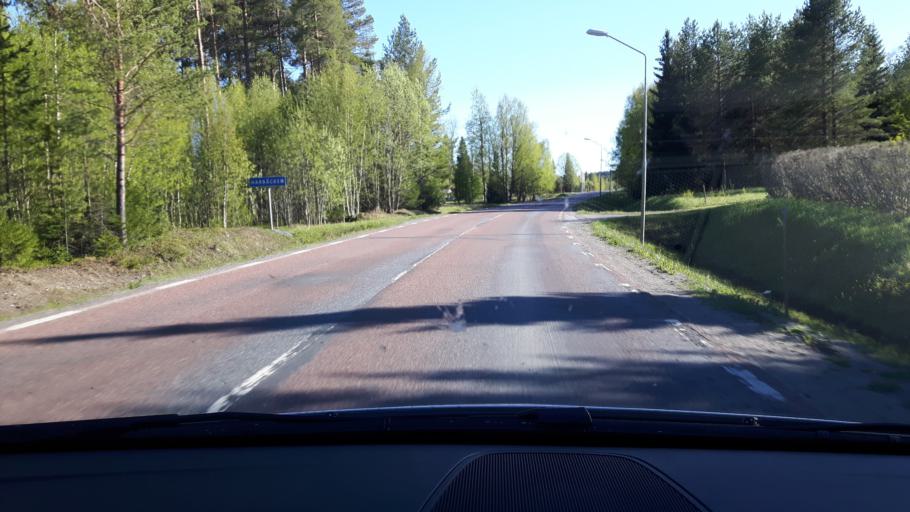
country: SE
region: Jaemtland
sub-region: Stroemsunds Kommun
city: Stroemsund
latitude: 63.8405
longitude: 15.5242
